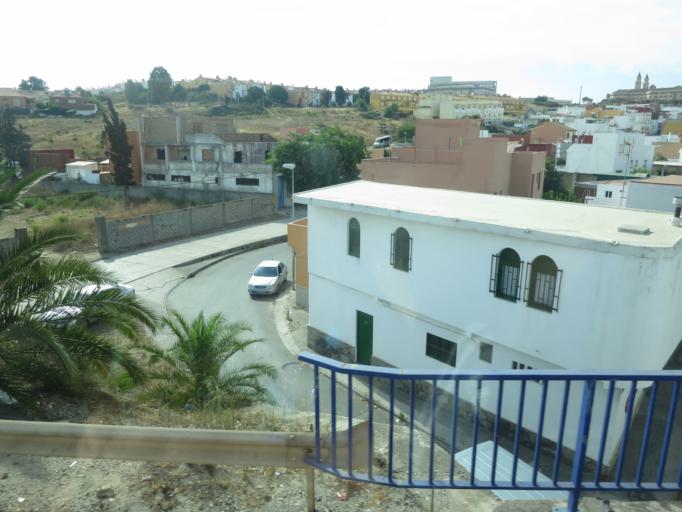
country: ES
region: Andalusia
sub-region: Provincia de Cadiz
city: Algeciras
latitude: 36.1154
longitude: -5.4468
